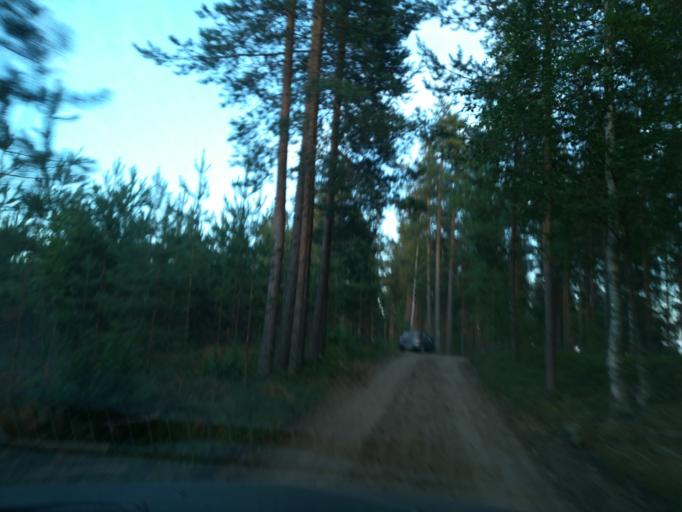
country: FI
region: South Karelia
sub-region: Lappeenranta
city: Joutseno
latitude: 61.3360
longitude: 28.3998
